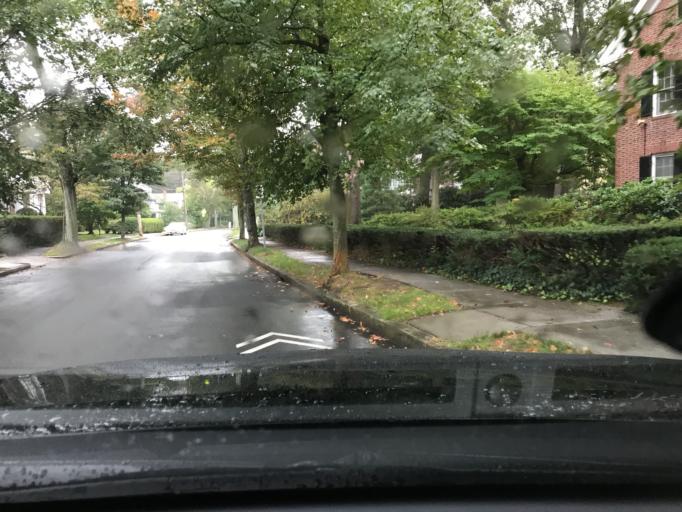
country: US
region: Massachusetts
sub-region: Norfolk County
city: Brookline
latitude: 42.3352
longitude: -71.1402
